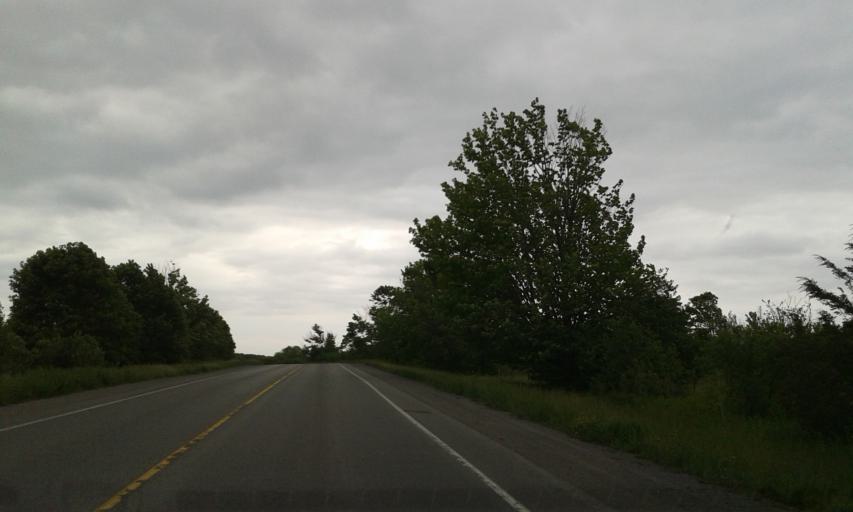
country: CA
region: Ontario
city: Quinte West
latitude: 43.9653
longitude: -77.5004
